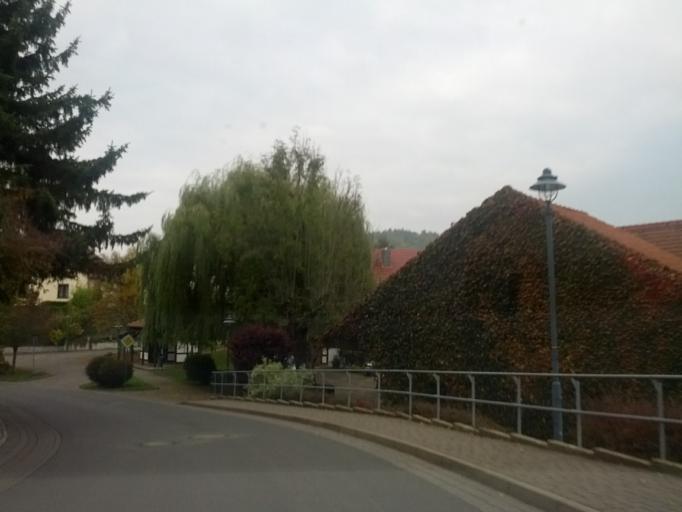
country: DE
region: Hesse
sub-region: Regierungsbezirk Kassel
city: Herleshausen
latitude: 50.9966
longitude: 10.2139
